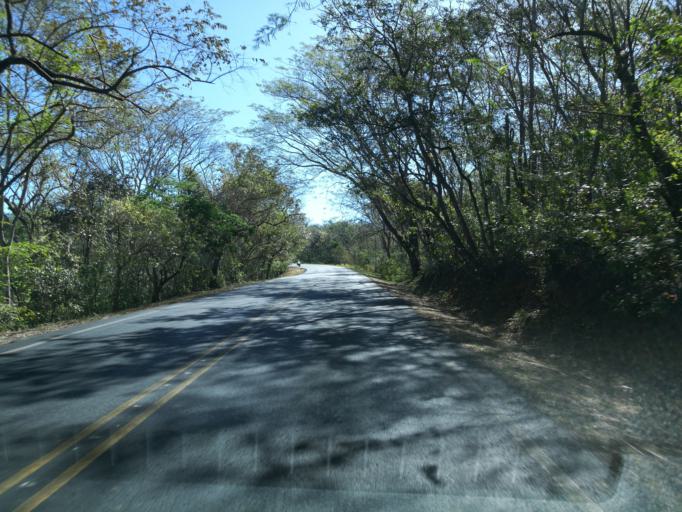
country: CR
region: Puntarenas
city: Miramar
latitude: 10.0874
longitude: -84.8373
